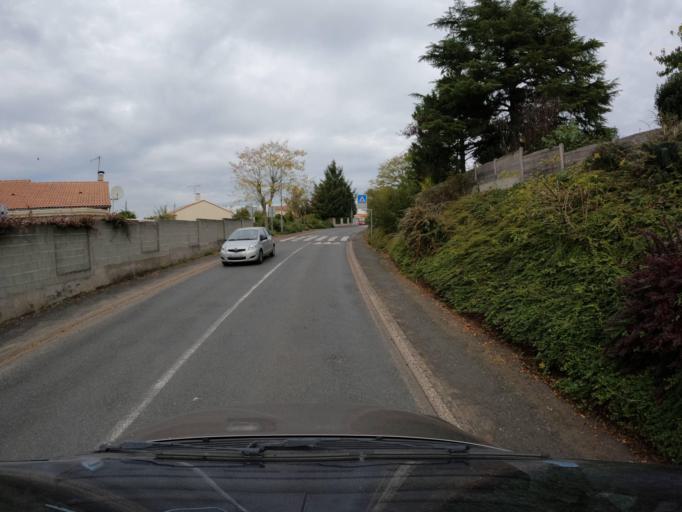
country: FR
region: Pays de la Loire
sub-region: Departement de Maine-et-Loire
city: Saint-Christophe-du-Bois
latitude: 47.0324
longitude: -0.9412
